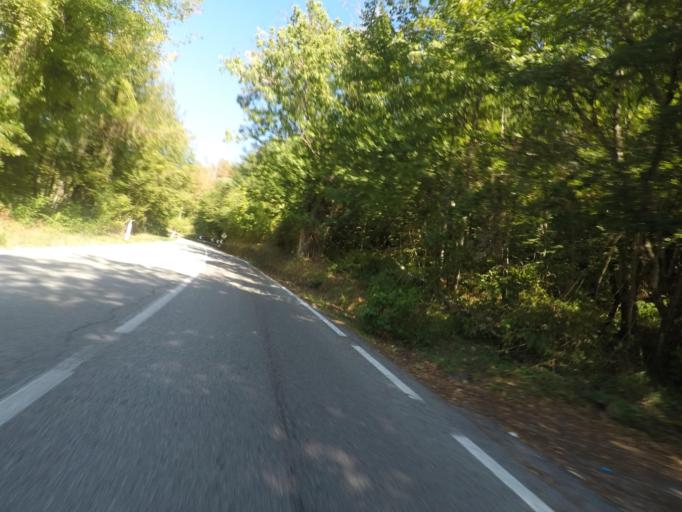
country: IT
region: Tuscany
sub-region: Provincia di Massa-Carrara
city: Fivizzano
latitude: 44.2421
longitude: 10.1460
